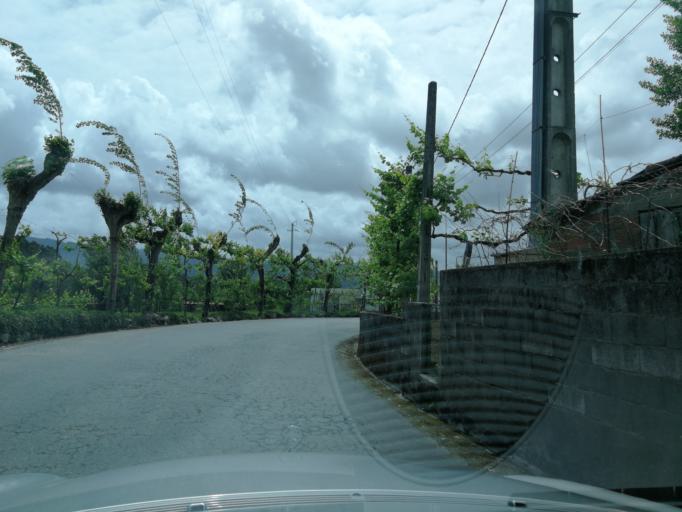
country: PT
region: Braga
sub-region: Braga
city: Adaufe
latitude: 41.6212
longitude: -8.3931
